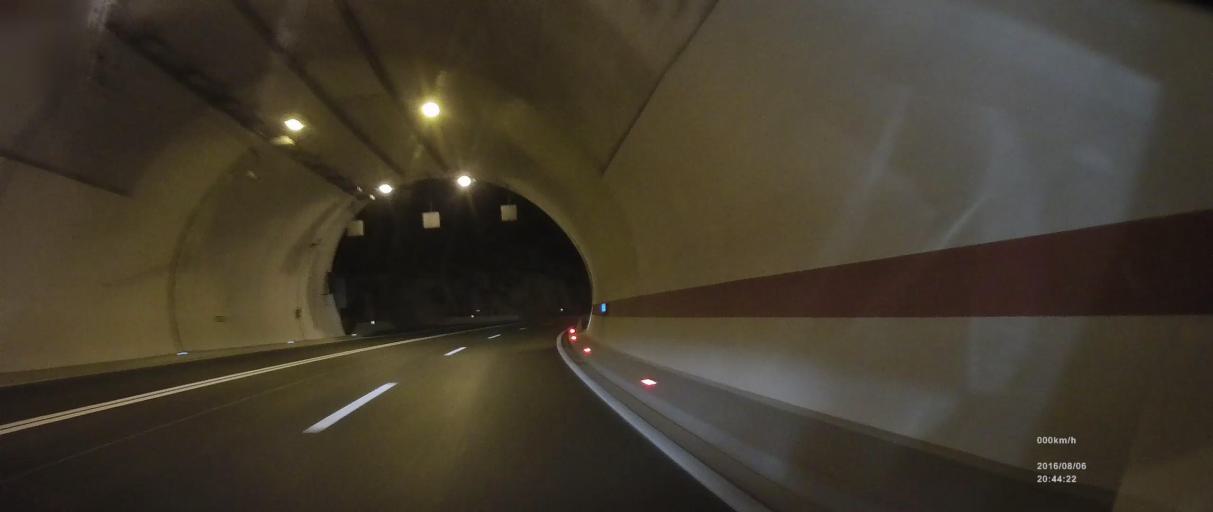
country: HR
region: Dubrovacko-Neretvanska
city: Komin
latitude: 43.0534
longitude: 17.4598
